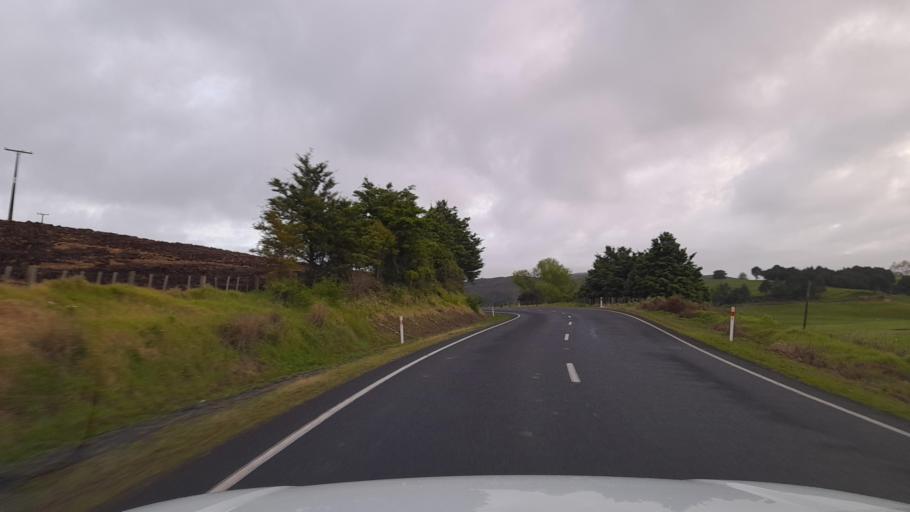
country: NZ
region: Northland
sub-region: Whangarei
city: Maungatapere
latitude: -35.7089
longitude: 174.0260
